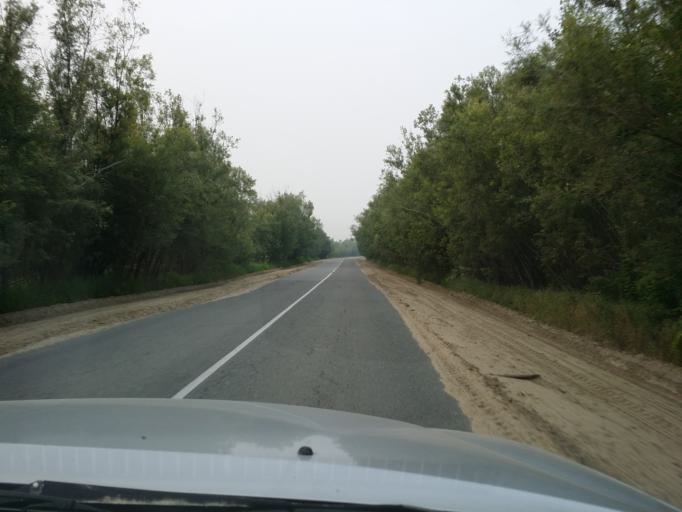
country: RU
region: Khanty-Mansiyskiy Avtonomnyy Okrug
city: Megion
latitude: 60.9994
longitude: 76.3041
